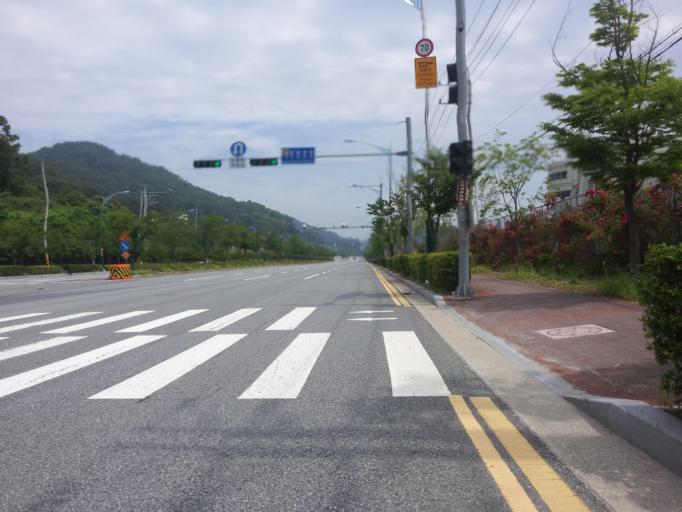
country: KR
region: Daejeon
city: Daejeon
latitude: 36.3225
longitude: 127.4723
